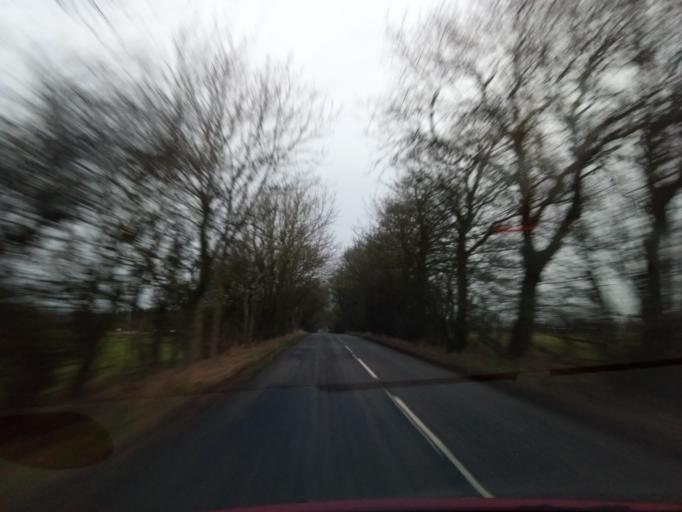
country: GB
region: England
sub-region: Northumberland
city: Rothley
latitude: 55.1956
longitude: -1.9721
